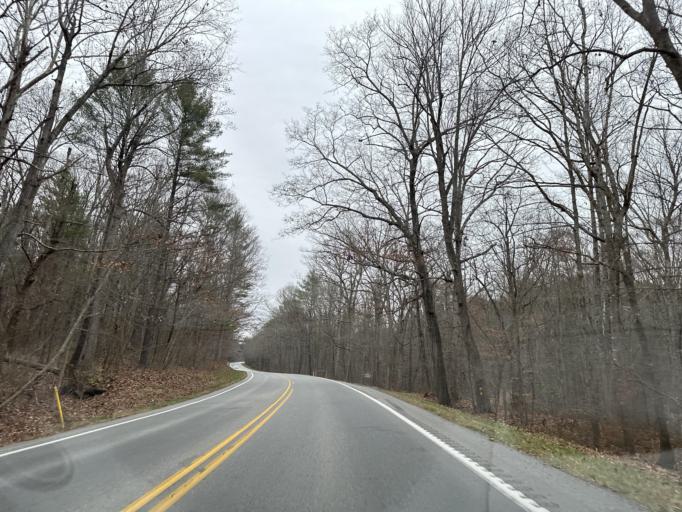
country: US
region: Virginia
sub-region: City of Staunton
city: Staunton
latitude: 38.1423
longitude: -79.2796
